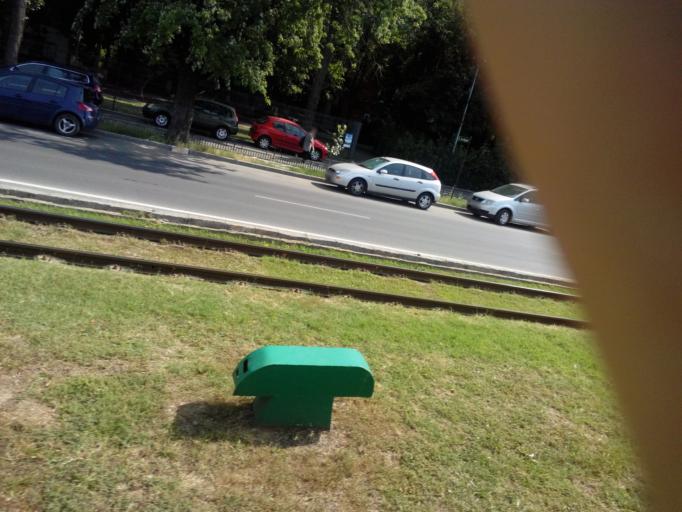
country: RO
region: Ilfov
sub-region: Comuna Chiajna
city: Rosu
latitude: 44.4283
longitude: 26.0472
